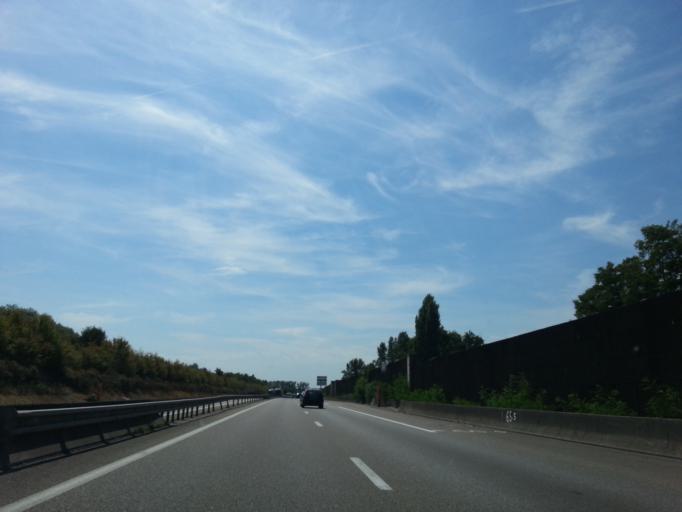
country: FR
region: Alsace
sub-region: Departement du Haut-Rhin
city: Horbourg-Wihr
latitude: 48.0781
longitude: 7.3849
